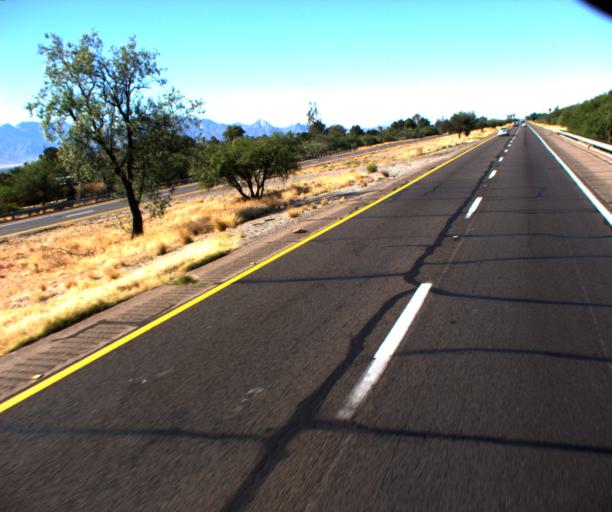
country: US
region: Arizona
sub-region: Pima County
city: Green Valley
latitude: 31.8788
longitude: -110.9893
